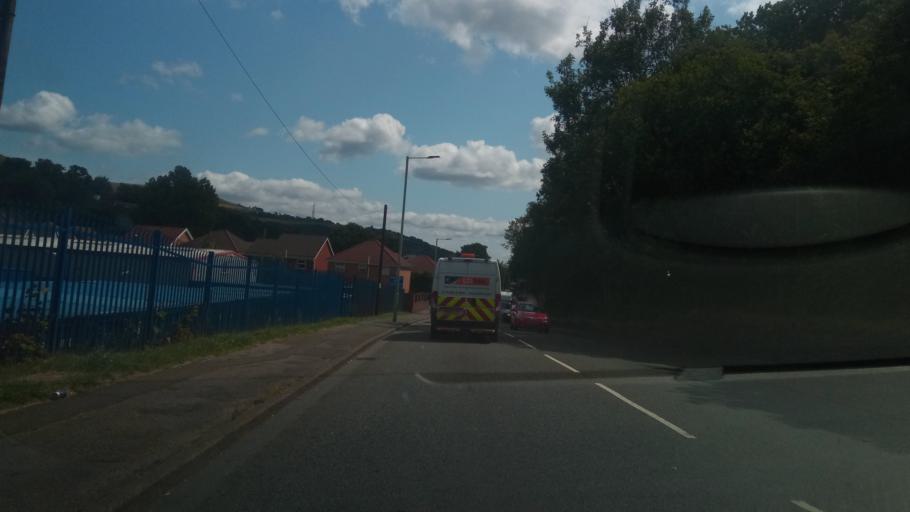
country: GB
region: Wales
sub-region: Rhondda Cynon Taf
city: Tonypandy
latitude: 51.6157
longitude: -3.4319
